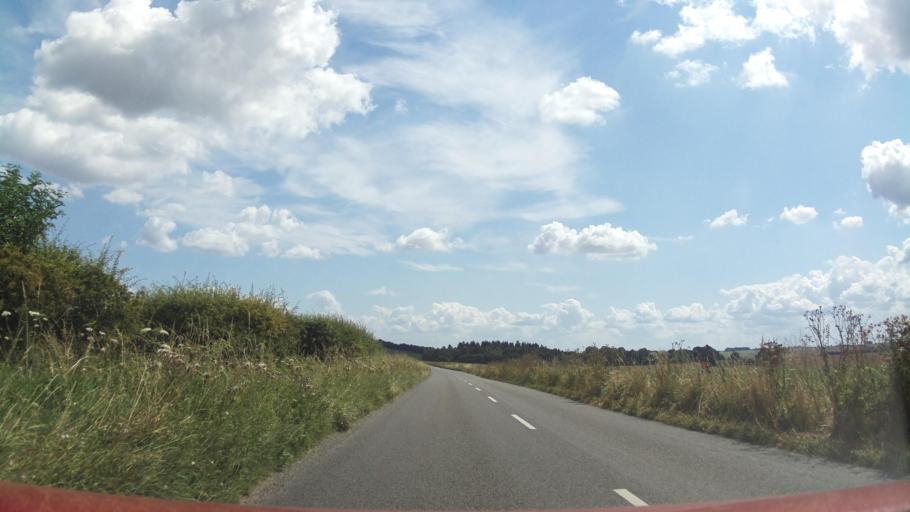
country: GB
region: England
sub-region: Borough of Swindon
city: Bishopstone
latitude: 51.5562
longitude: -1.6060
